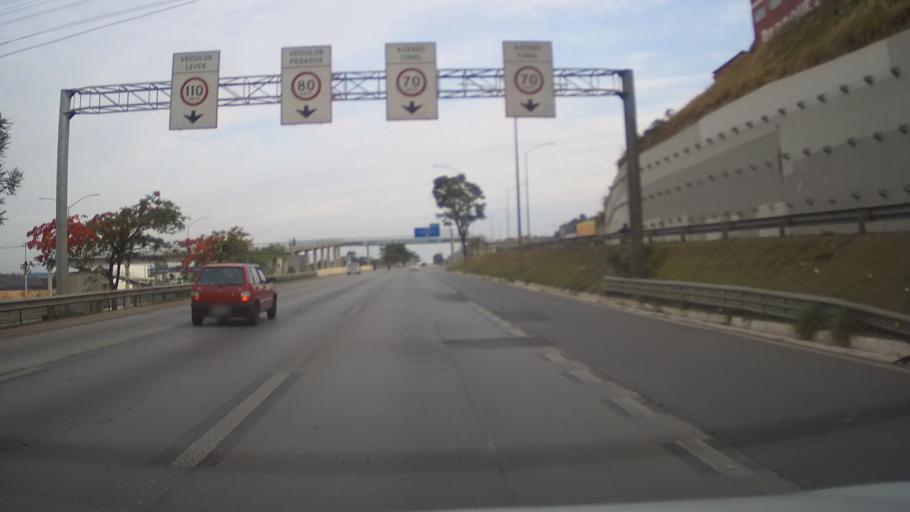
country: BR
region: Minas Gerais
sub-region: Santa Luzia
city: Santa Luzia
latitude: -19.7957
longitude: -43.9495
